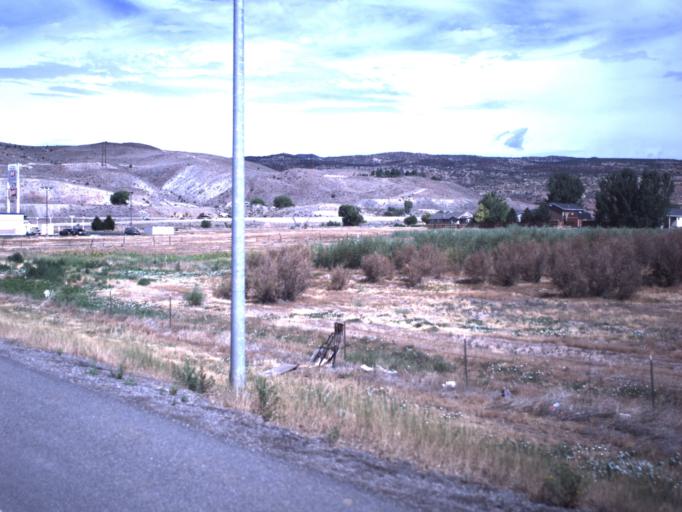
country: US
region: Utah
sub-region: Sevier County
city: Richfield
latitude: 38.7500
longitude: -112.0987
